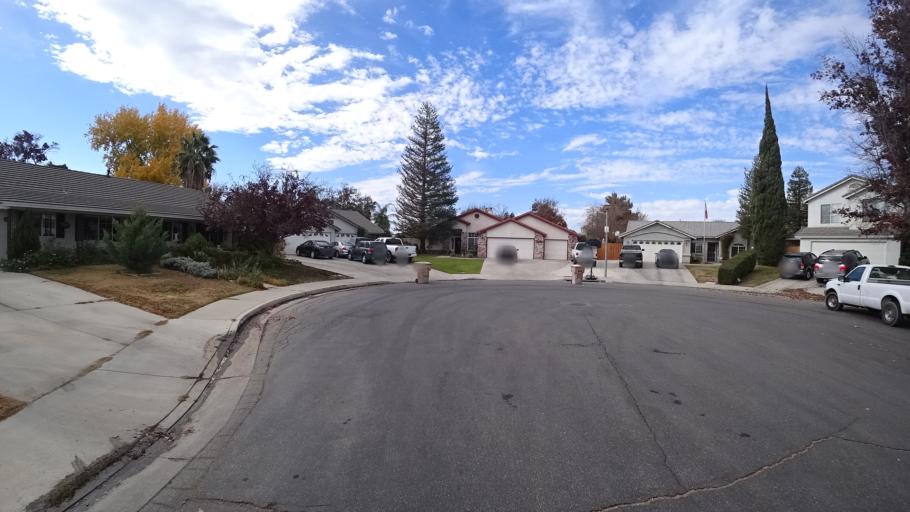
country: US
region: California
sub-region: Kern County
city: Rosedale
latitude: 35.3970
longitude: -119.1358
